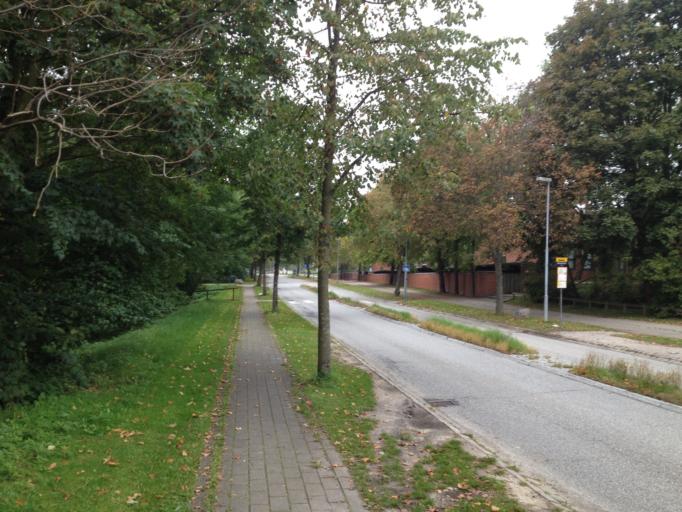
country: DK
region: Capital Region
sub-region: Fredensborg Kommune
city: Niva
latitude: 55.9328
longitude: 12.5019
